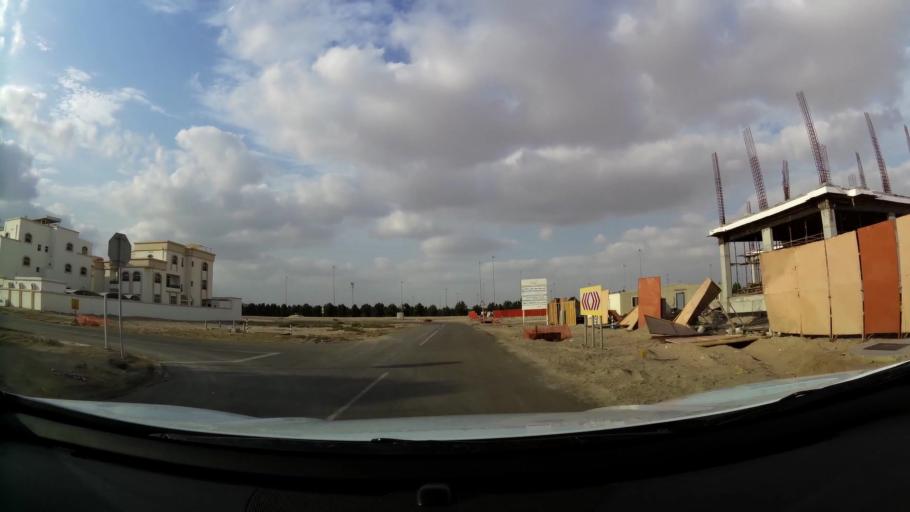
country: AE
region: Abu Dhabi
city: Abu Dhabi
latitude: 24.3722
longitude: 54.5498
